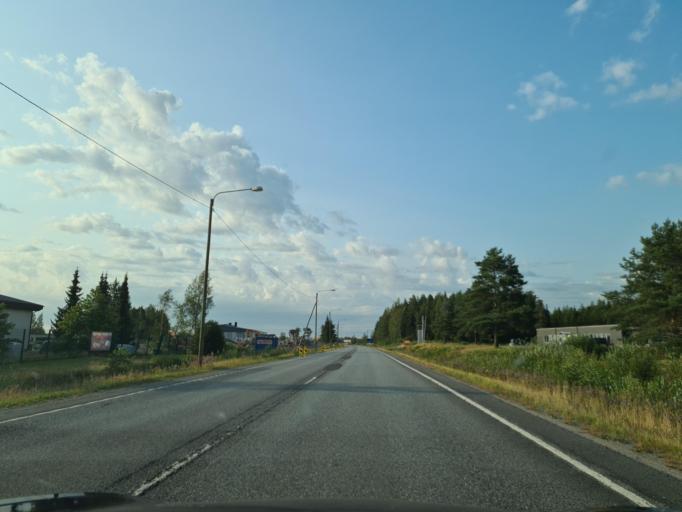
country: FI
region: Southern Ostrobothnia
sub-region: Seinaejoki
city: Kauhava
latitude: 63.0823
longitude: 23.0587
